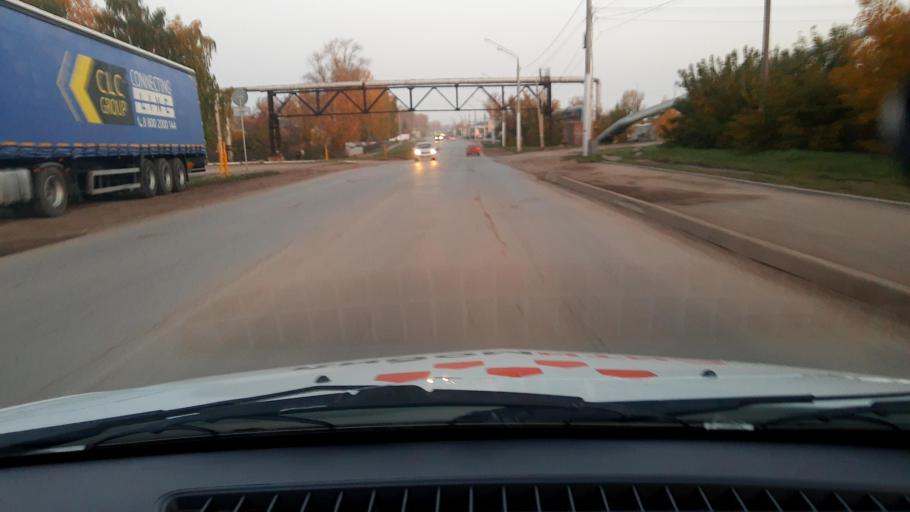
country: RU
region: Bashkortostan
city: Iglino
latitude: 54.7622
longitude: 56.2413
